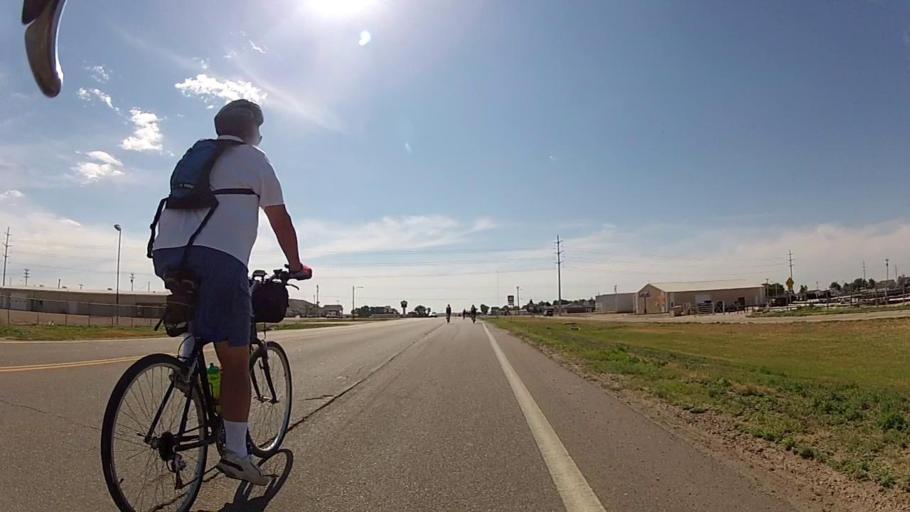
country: US
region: Kansas
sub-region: Grant County
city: Ulysses
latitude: 37.5755
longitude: -101.3468
